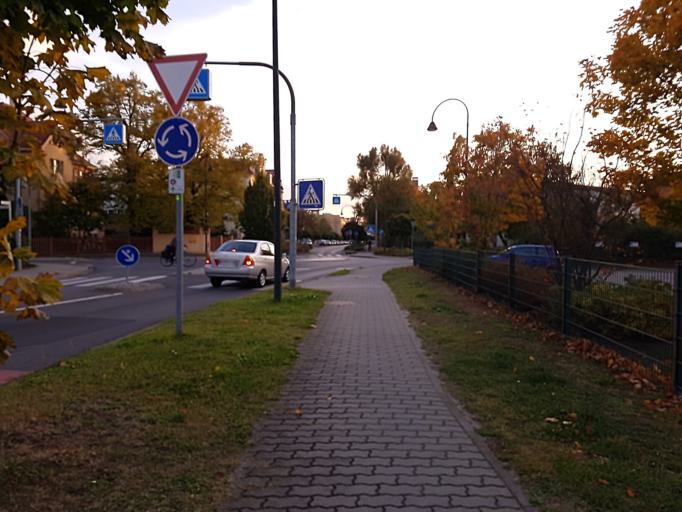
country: DE
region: Saxony-Anhalt
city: Wittenburg
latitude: 51.8707
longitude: 12.6586
